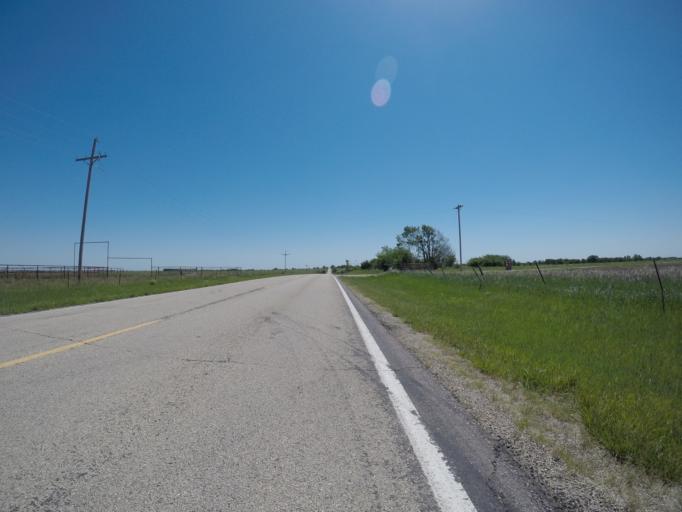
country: US
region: Kansas
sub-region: Shawnee County
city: Auburn
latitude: 38.8847
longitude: -95.9939
